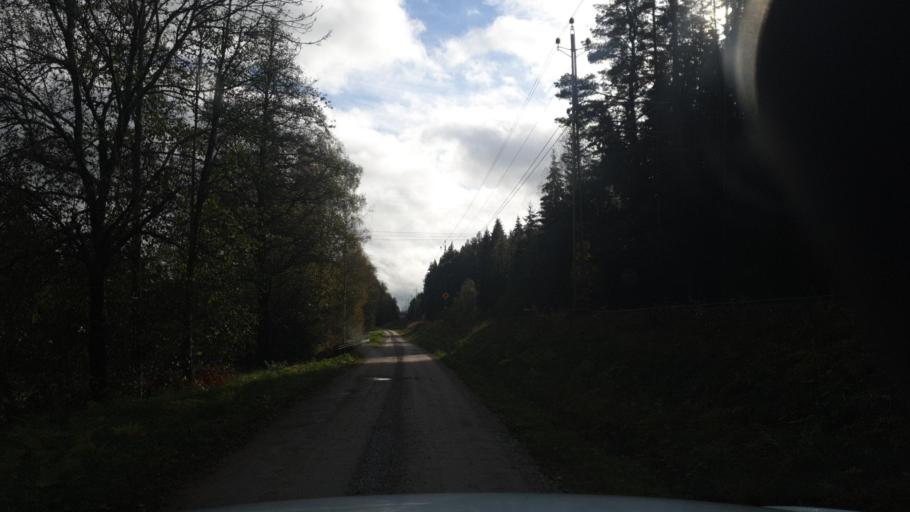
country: SE
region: Vaermland
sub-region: Karlstads Kommun
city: Edsvalla
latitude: 59.6138
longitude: 12.9752
